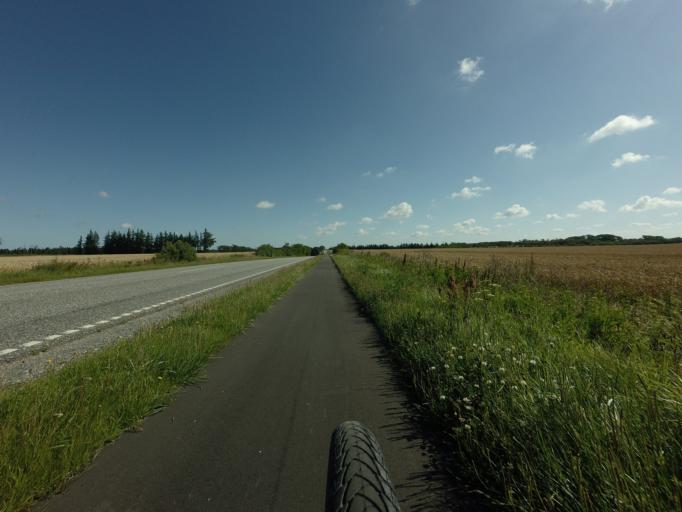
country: DK
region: North Denmark
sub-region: Hjorring Kommune
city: Vra
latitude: 57.4156
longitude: 9.8243
